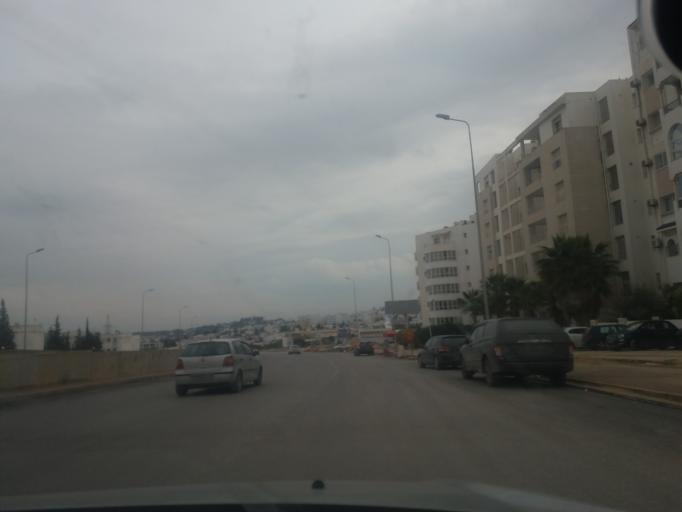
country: TN
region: Tunis
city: Tunis
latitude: 36.8541
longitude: 10.1525
